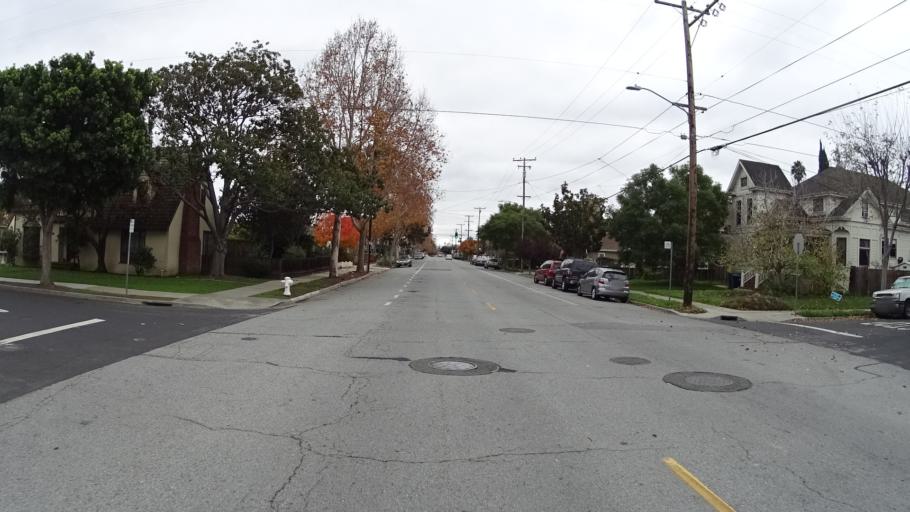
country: US
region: California
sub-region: Santa Clara County
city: Santa Clara
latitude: 37.3458
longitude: -121.9466
